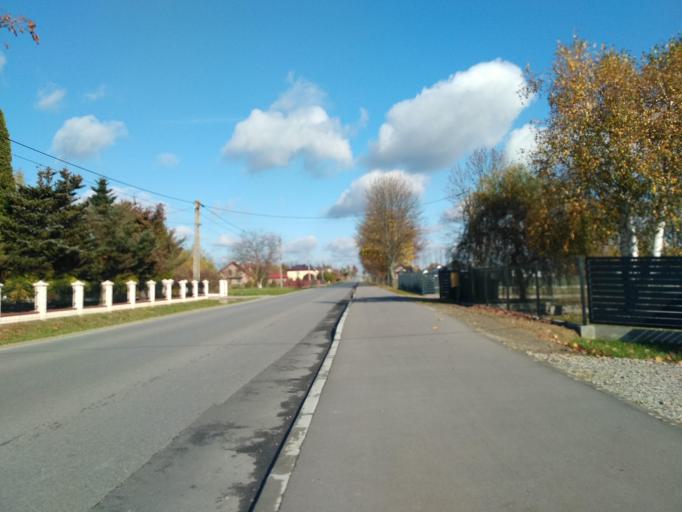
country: PL
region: Subcarpathian Voivodeship
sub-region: Powiat rzeszowski
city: Trzciana
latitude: 50.0975
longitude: 21.8505
